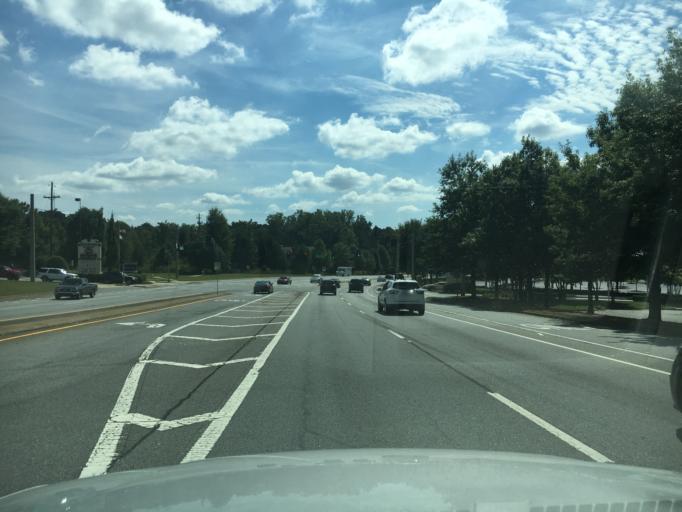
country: US
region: Georgia
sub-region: Gwinnett County
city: Duluth
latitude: 33.9967
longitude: -84.0923
